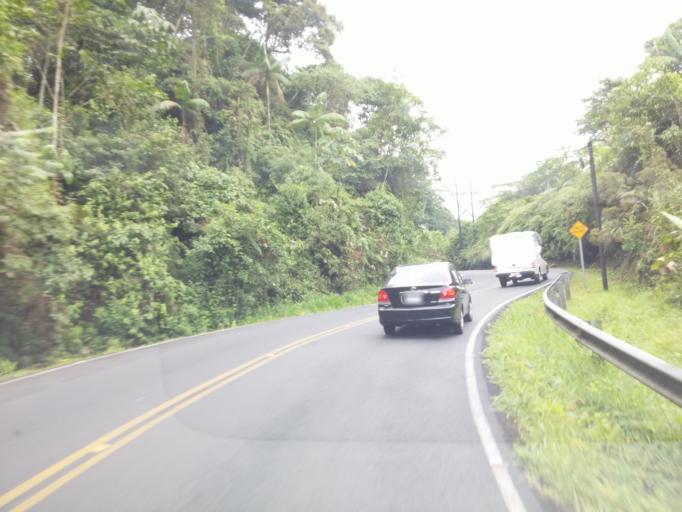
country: CR
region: Alajuela
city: San Ramon
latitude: 10.2202
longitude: -84.5424
